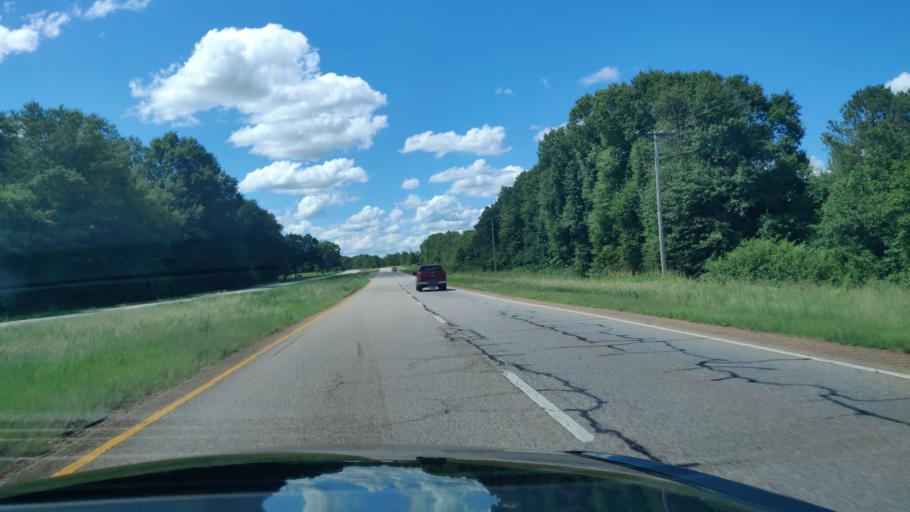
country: US
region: Georgia
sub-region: Stewart County
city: Richland
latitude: 32.0025
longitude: -84.6478
